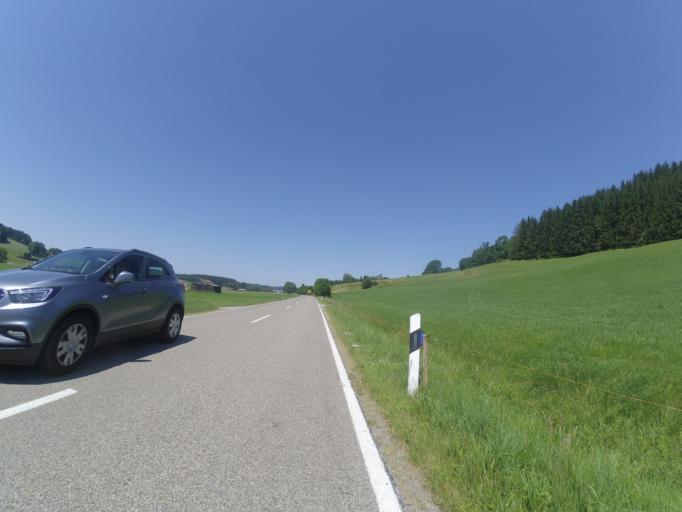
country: DE
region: Bavaria
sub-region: Swabia
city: Bohen
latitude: 47.8798
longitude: 10.3344
